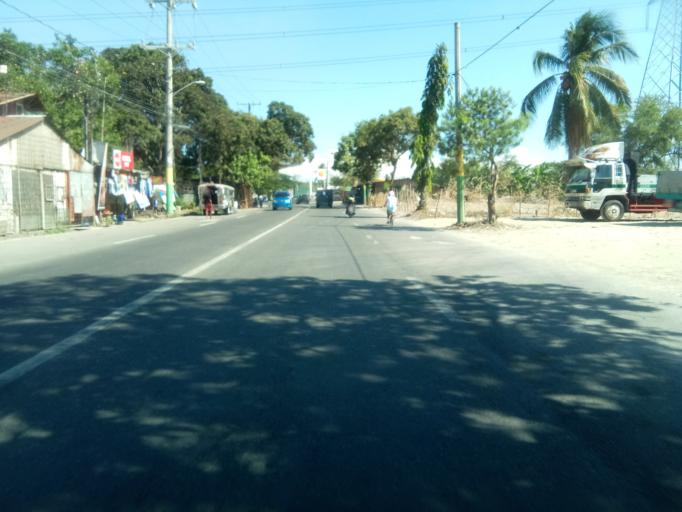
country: PH
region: Calabarzon
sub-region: Province of Cavite
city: Bulihan
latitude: 14.3162
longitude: 120.9863
